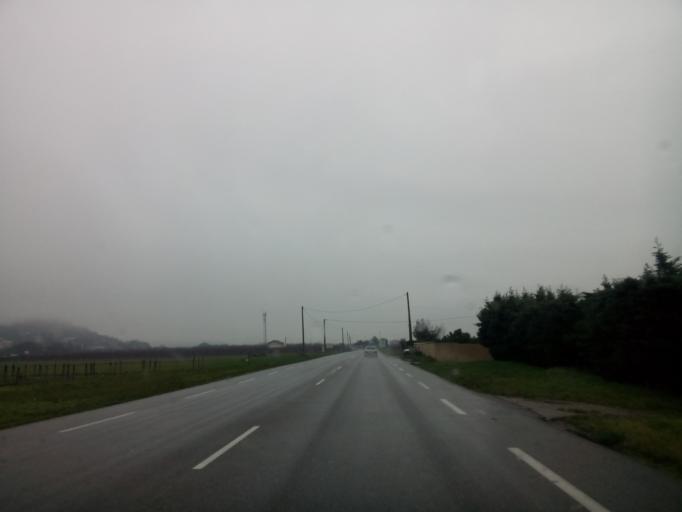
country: FR
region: Rhone-Alpes
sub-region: Departement de la Drome
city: Clerieux
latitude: 45.0538
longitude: 4.9585
